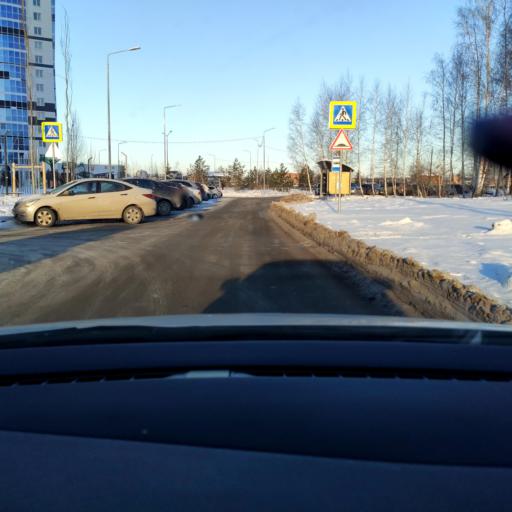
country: RU
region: Tatarstan
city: Stolbishchi
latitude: 55.6888
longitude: 49.2021
